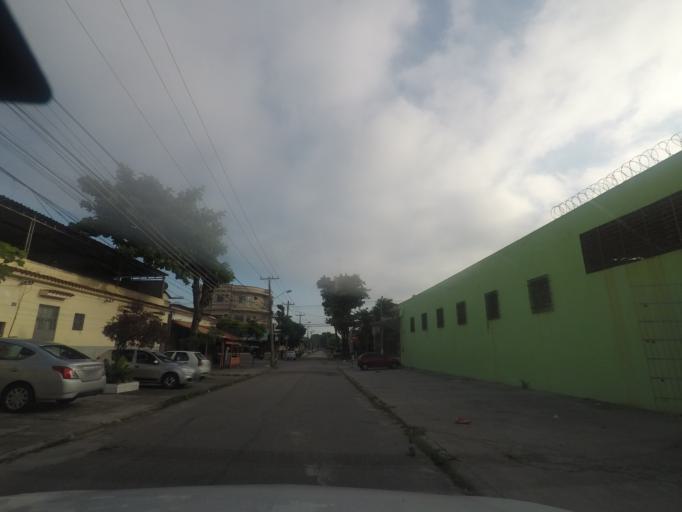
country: BR
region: Rio de Janeiro
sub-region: Duque De Caxias
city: Duque de Caxias
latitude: -22.8385
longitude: -43.2726
